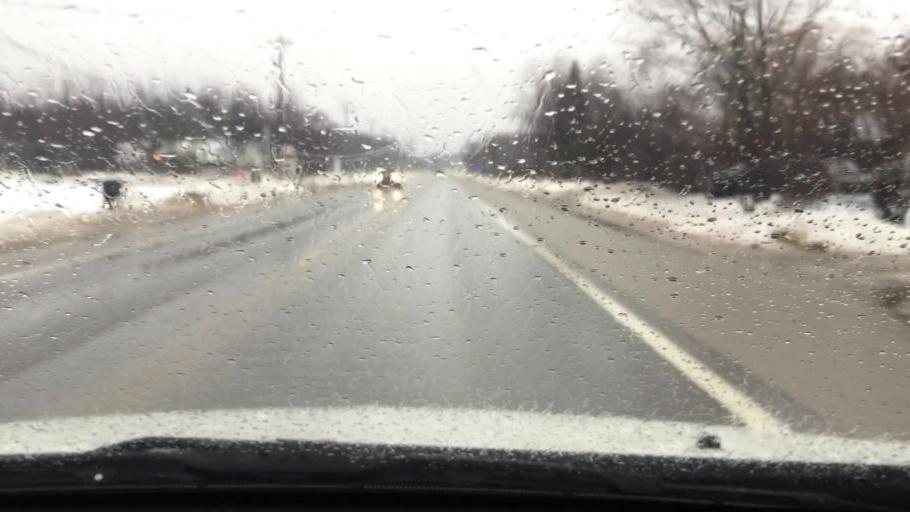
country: US
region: Michigan
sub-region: Charlevoix County
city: Charlevoix
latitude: 45.2918
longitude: -85.2492
